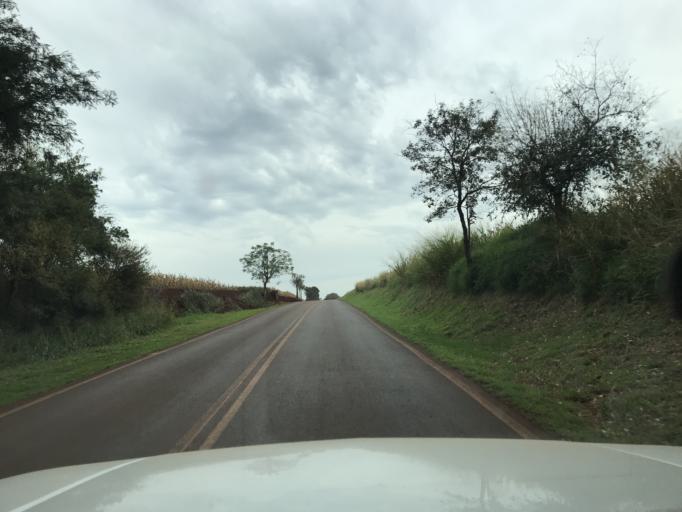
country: BR
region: Parana
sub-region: Palotina
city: Palotina
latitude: -24.4326
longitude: -53.9115
